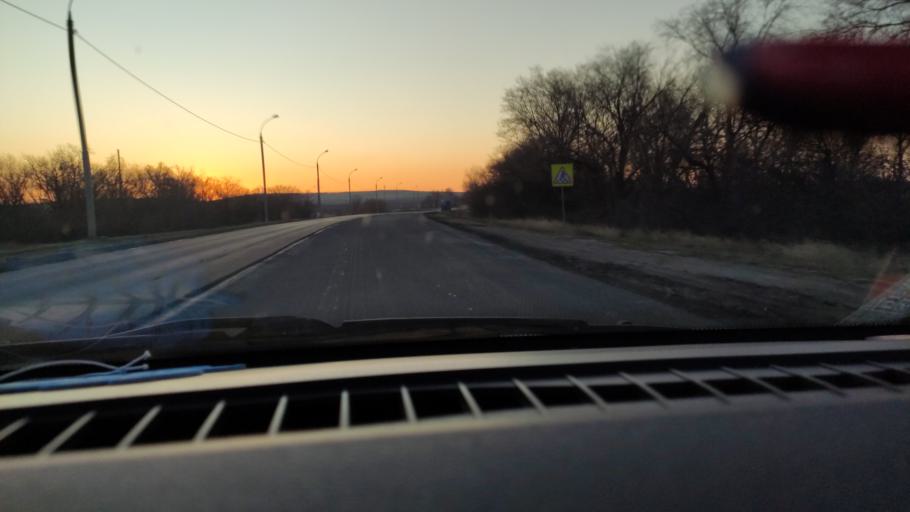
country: RU
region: Saratov
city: Yelshanka
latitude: 51.8306
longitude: 46.2337
